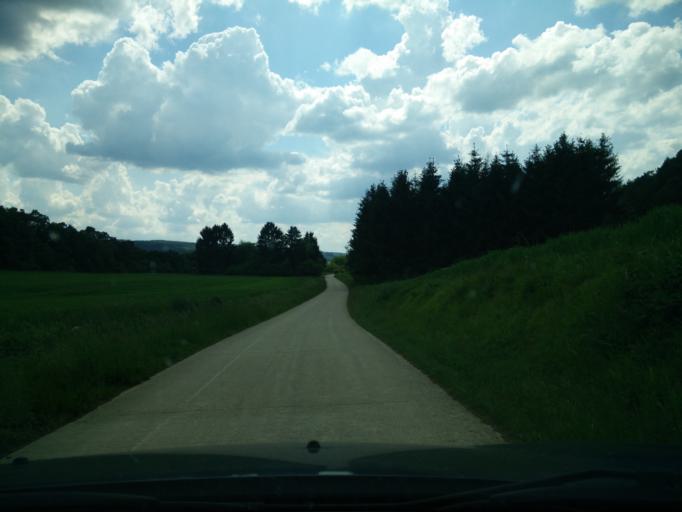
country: FR
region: Champagne-Ardenne
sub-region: Departement des Ardennes
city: Vireux-Molhain
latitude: 50.0799
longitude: 4.6132
